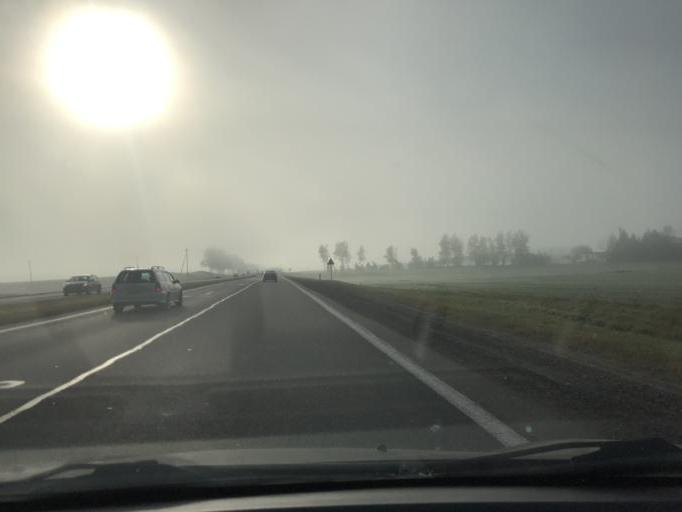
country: BY
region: Minsk
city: Luhavaya Slabada
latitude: 53.7463
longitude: 27.8370
